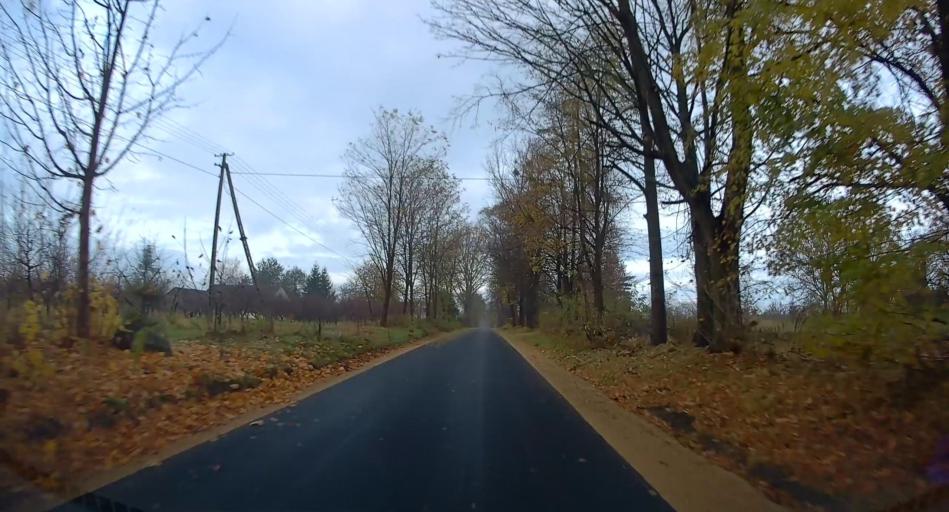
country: PL
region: Lodz Voivodeship
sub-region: Powiat skierniewicki
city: Kowiesy
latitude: 51.9234
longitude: 20.4103
